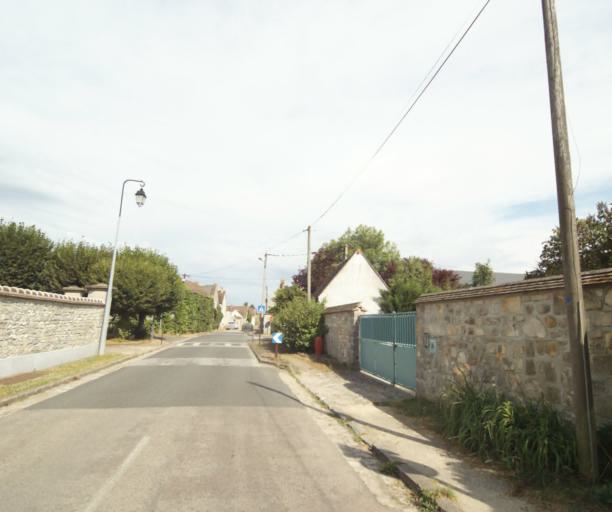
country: FR
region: Ile-de-France
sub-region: Departement de Seine-et-Marne
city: Acheres-la-Foret
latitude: 48.3557
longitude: 2.5667
